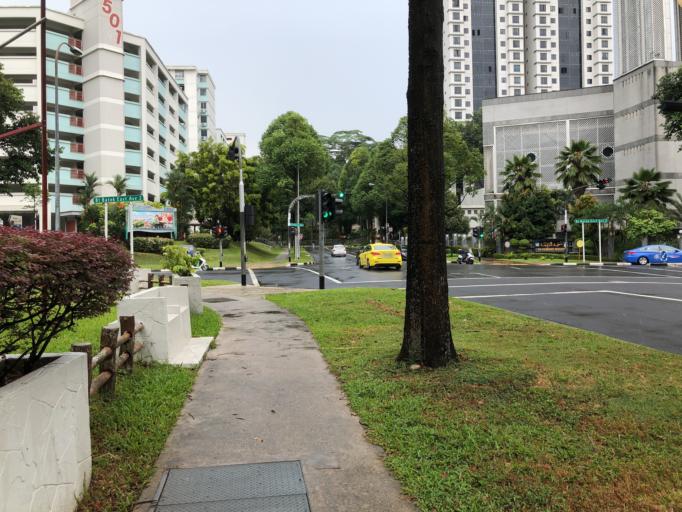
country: SG
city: Singapore
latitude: 1.3509
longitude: 103.7555
